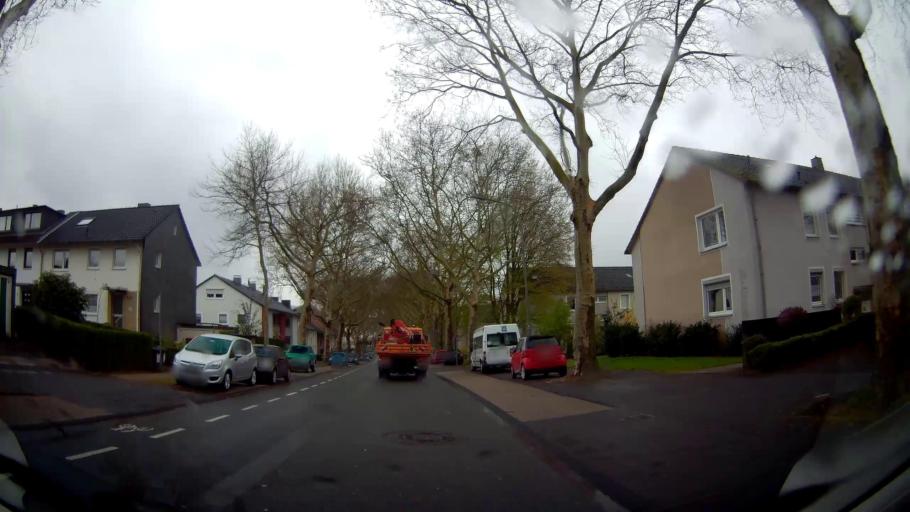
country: DE
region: North Rhine-Westphalia
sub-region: Regierungsbezirk Arnsberg
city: Herne
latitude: 51.5153
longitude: 7.2696
